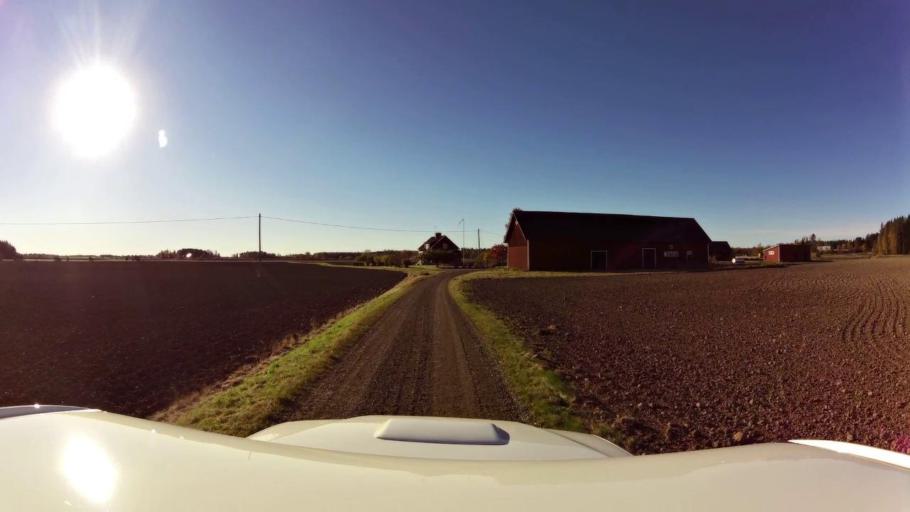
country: SE
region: OEstergoetland
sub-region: Linkopings Kommun
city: Ljungsbro
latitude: 58.5128
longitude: 15.3962
